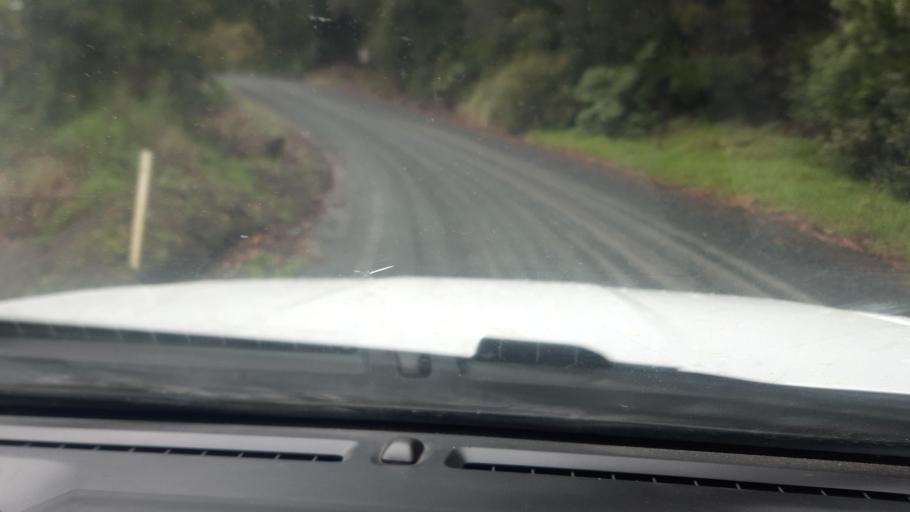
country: NZ
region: Northland
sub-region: Far North District
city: Kaitaia
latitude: -34.9796
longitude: 173.2029
